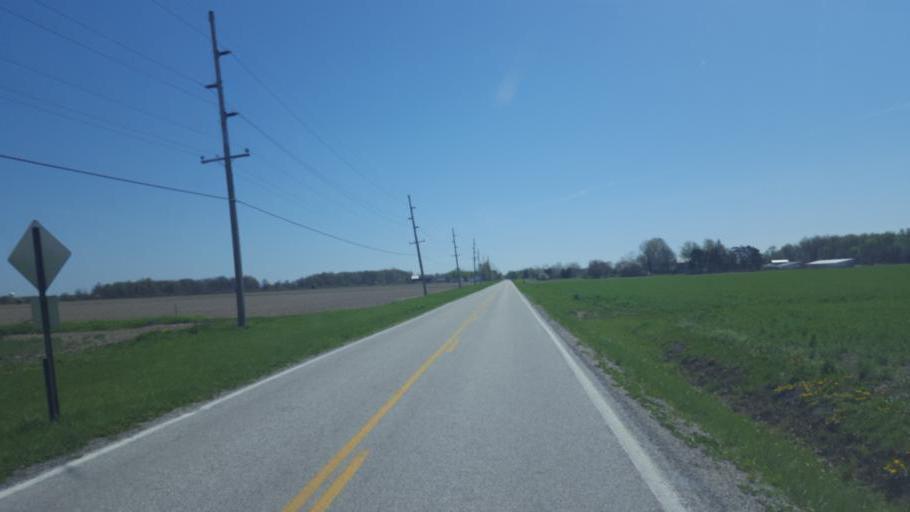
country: US
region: Ohio
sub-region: Ottawa County
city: Oak Harbor
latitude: 41.4939
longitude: -83.1241
